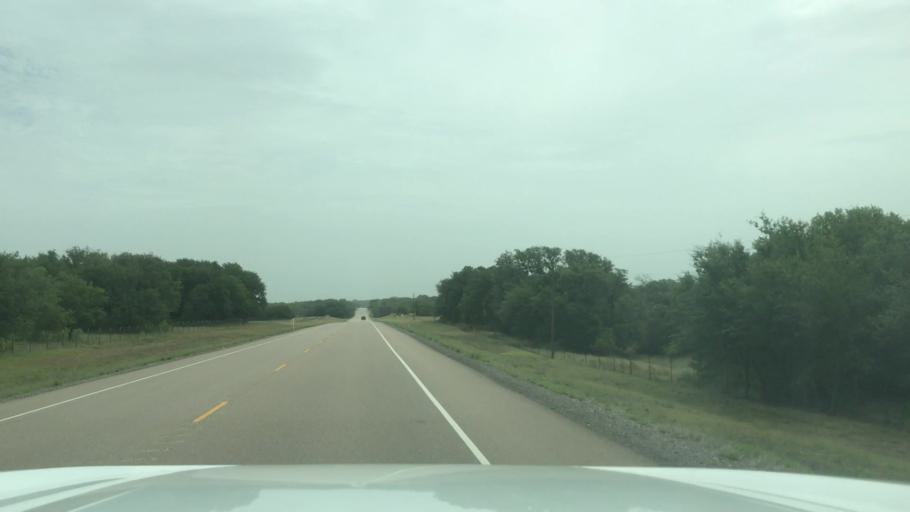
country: US
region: Texas
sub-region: Hamilton County
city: Hico
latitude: 31.9779
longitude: -97.9052
